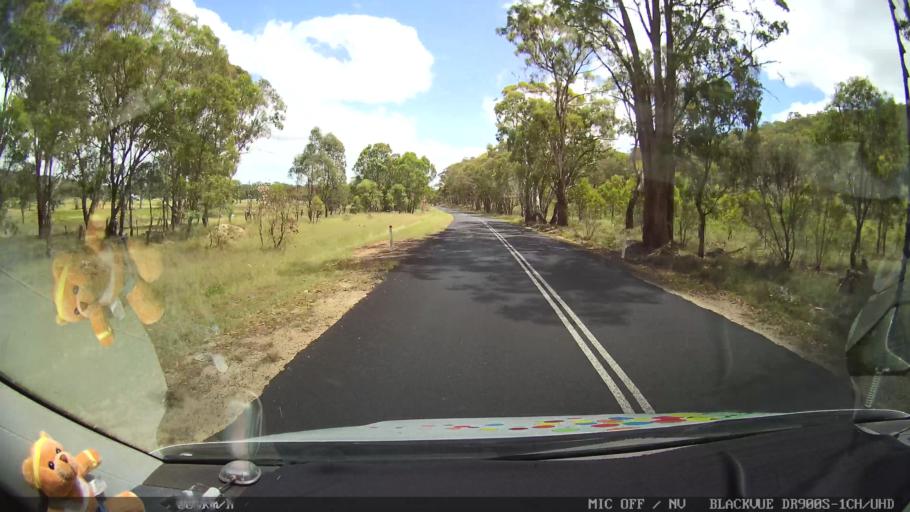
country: AU
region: New South Wales
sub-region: Glen Innes Severn
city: Glen Innes
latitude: -29.5326
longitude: 151.6736
